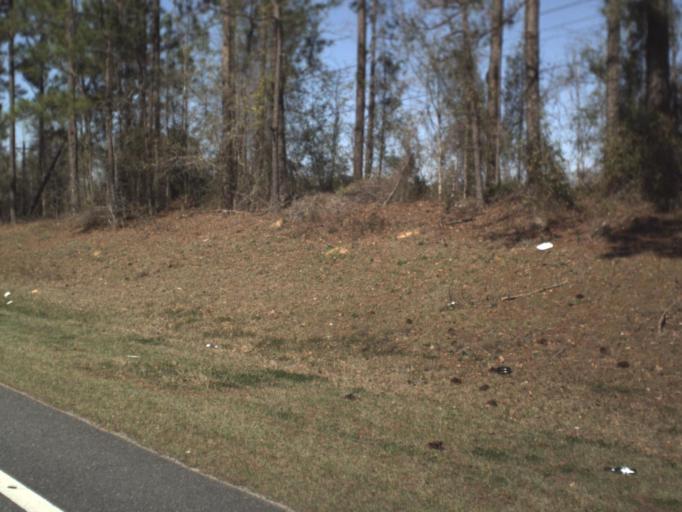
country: US
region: Florida
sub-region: Jackson County
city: Sneads
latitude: 30.7195
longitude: -85.0427
